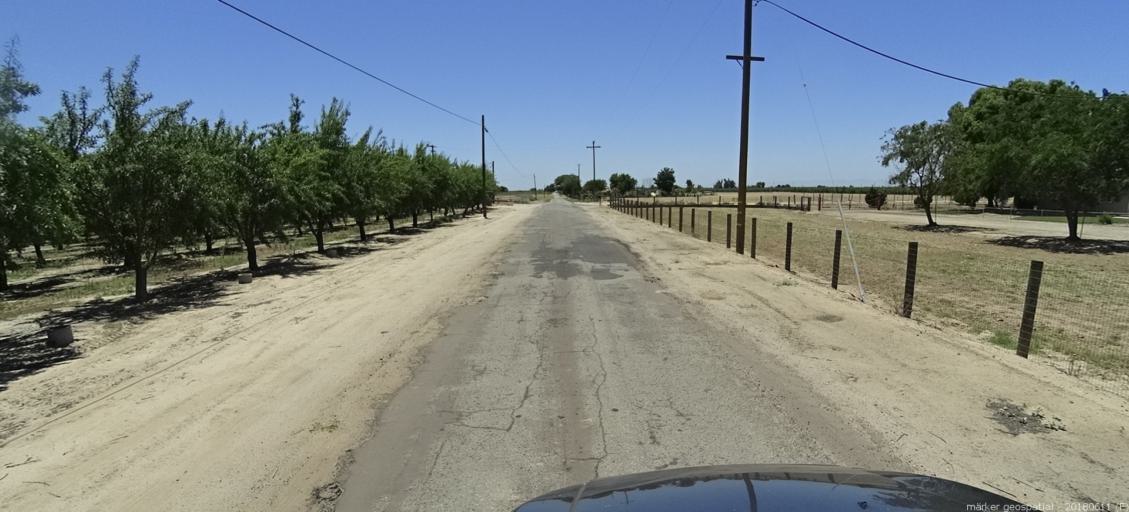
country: US
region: California
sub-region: Madera County
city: Fairmead
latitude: 37.0082
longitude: -120.1842
